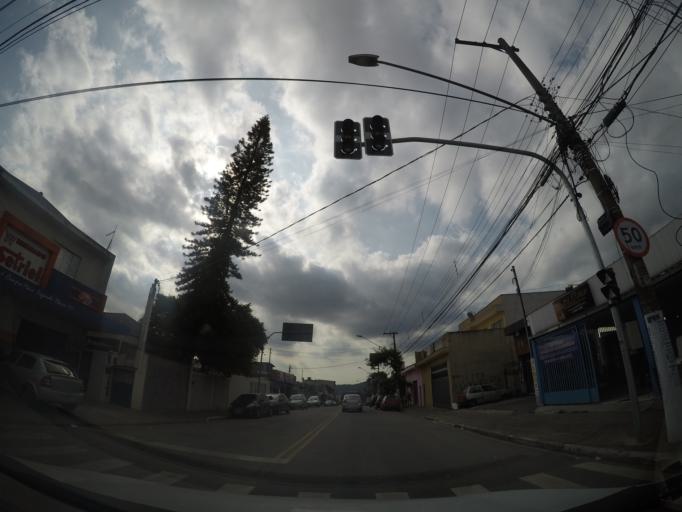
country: BR
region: Sao Paulo
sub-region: Guarulhos
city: Guarulhos
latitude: -23.4163
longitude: -46.4573
